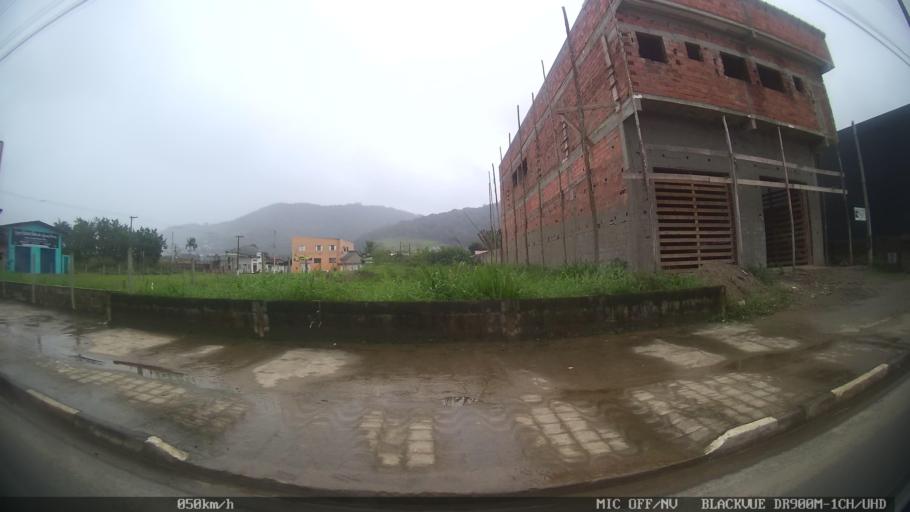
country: BR
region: Sao Paulo
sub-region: Juquia
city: Juquia
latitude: -24.3159
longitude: -47.6323
